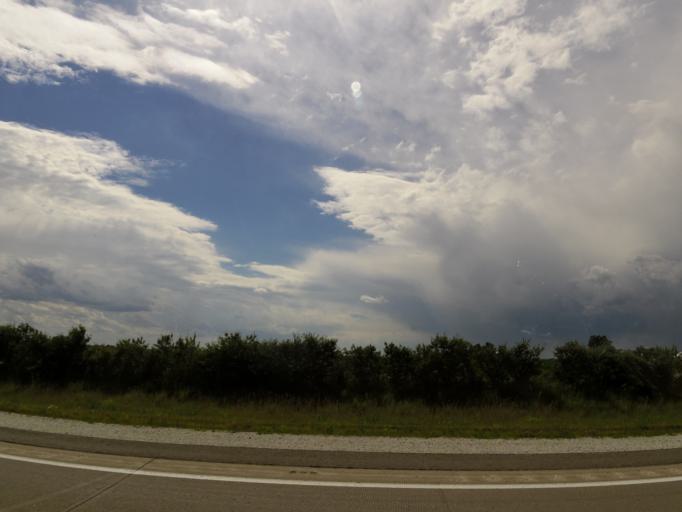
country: US
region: Iowa
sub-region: Henry County
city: Winfield
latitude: 41.1396
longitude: -91.5402
